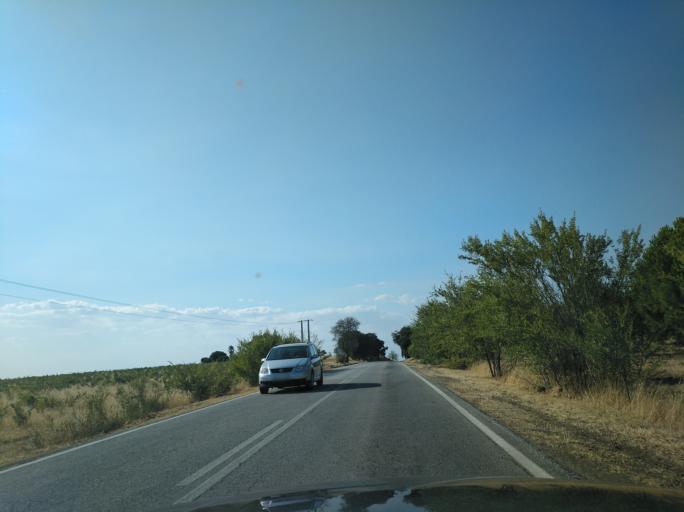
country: ES
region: Extremadura
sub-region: Provincia de Badajoz
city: Valencia del Mombuey
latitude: 38.2325
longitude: -7.2344
